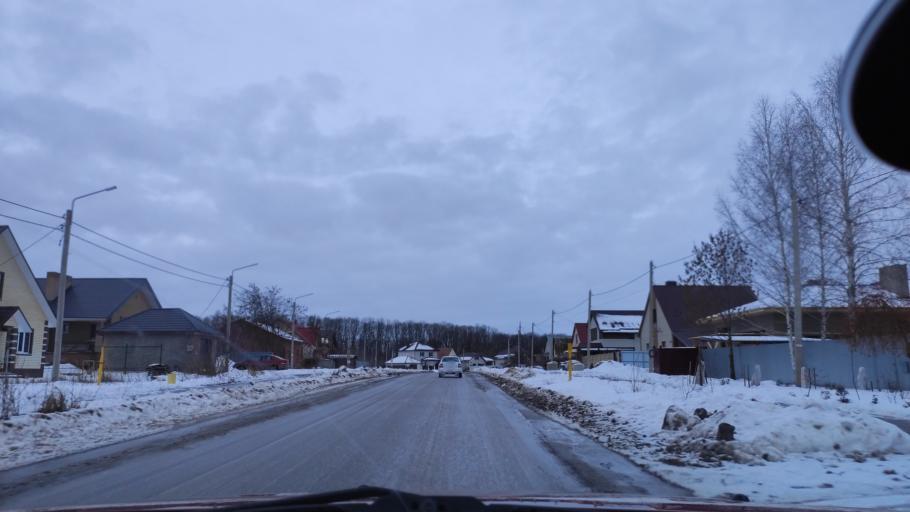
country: RU
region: Tambov
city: Tambov
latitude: 52.7599
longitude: 41.3735
